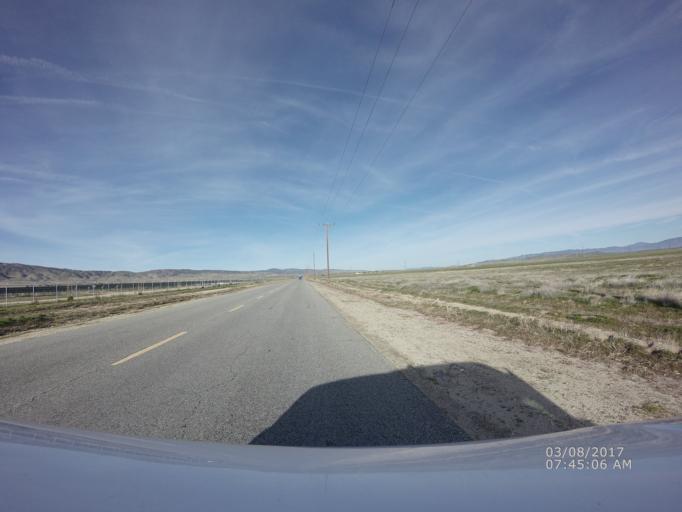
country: US
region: California
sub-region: Los Angeles County
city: Leona Valley
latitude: 34.7037
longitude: -118.3356
